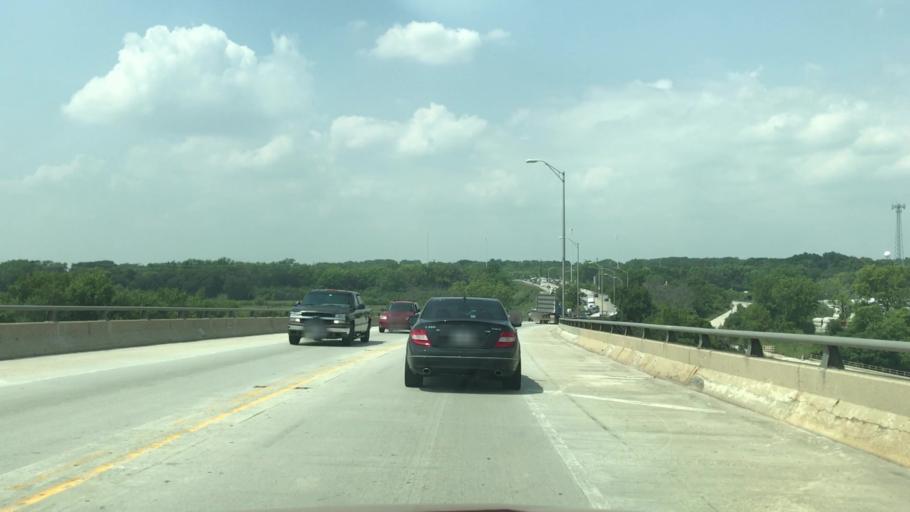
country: US
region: Illinois
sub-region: Will County
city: Lockport
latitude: 41.5915
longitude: -88.0680
